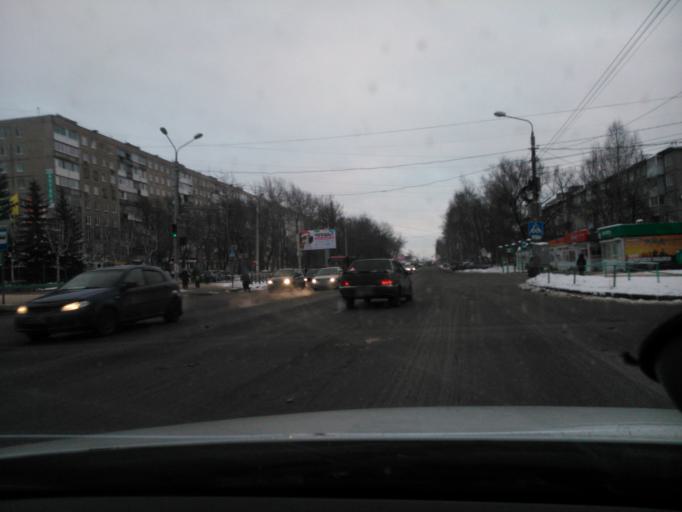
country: RU
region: Perm
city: Kondratovo
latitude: 57.9659
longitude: 56.1760
